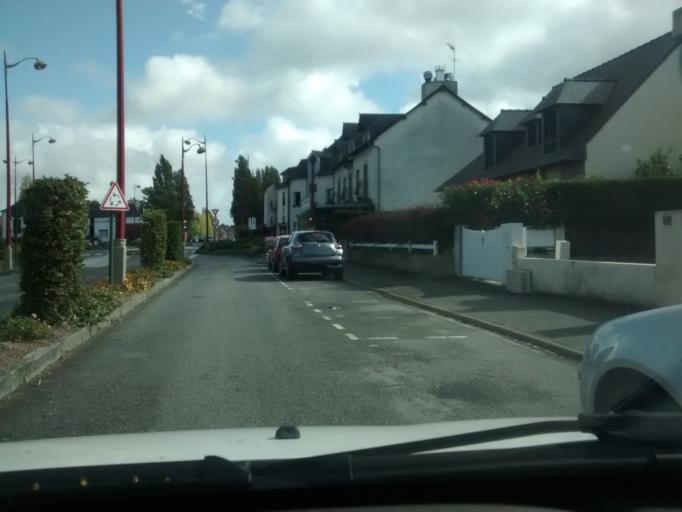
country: FR
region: Brittany
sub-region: Departement d'Ille-et-Vilaine
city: Cesson-Sevigne
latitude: 48.1142
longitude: -1.6113
